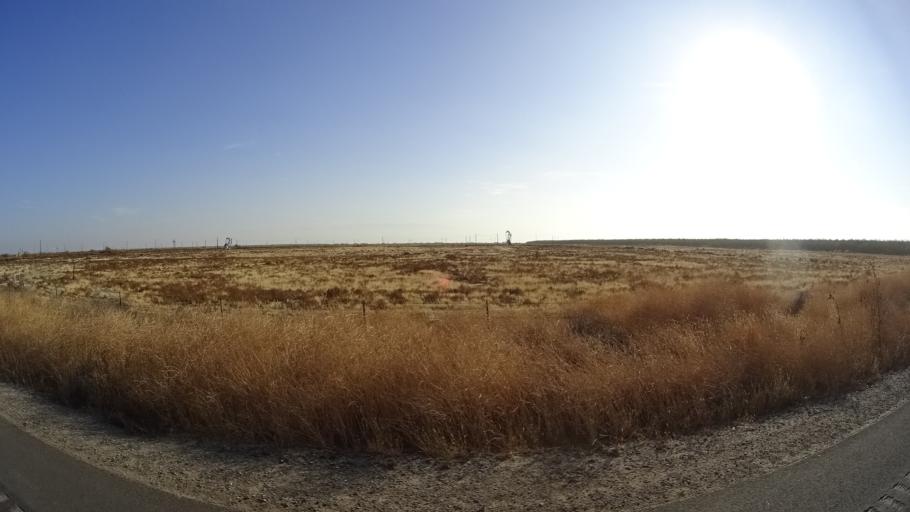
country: US
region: California
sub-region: Kern County
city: Rosedale
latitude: 35.2961
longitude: -119.2380
